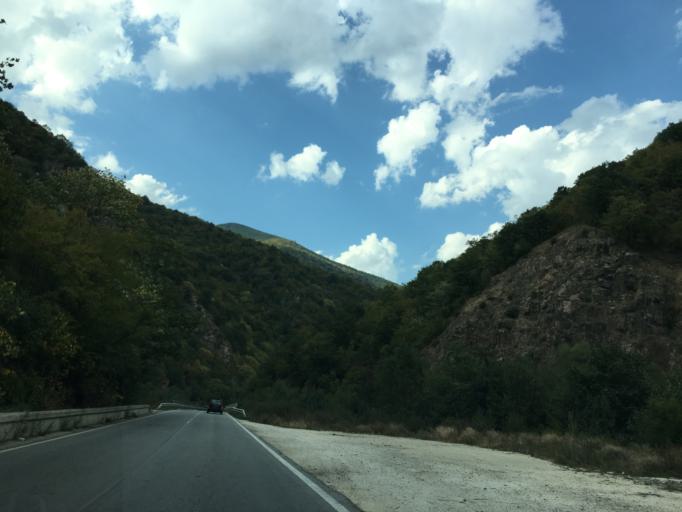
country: BG
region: Pazardzhik
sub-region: Obshtina Septemvri
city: Septemvri
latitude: 42.1244
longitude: 24.1237
